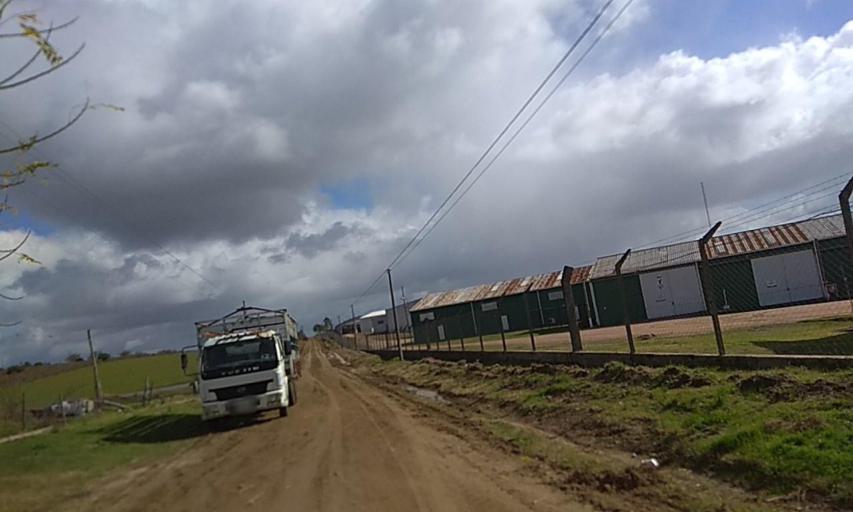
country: UY
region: Florida
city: Florida
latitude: -34.1143
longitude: -56.2279
